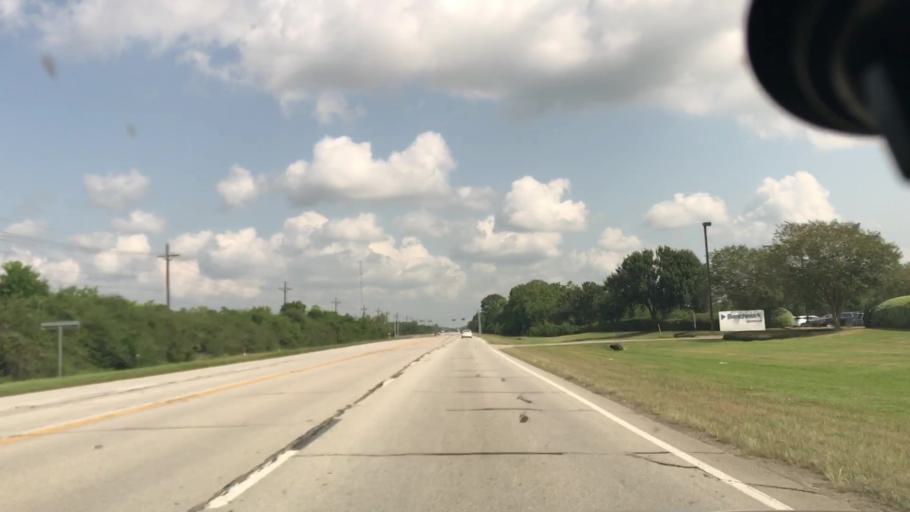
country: US
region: Texas
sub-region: Brazoria County
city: Angleton
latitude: 29.2060
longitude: -95.4357
